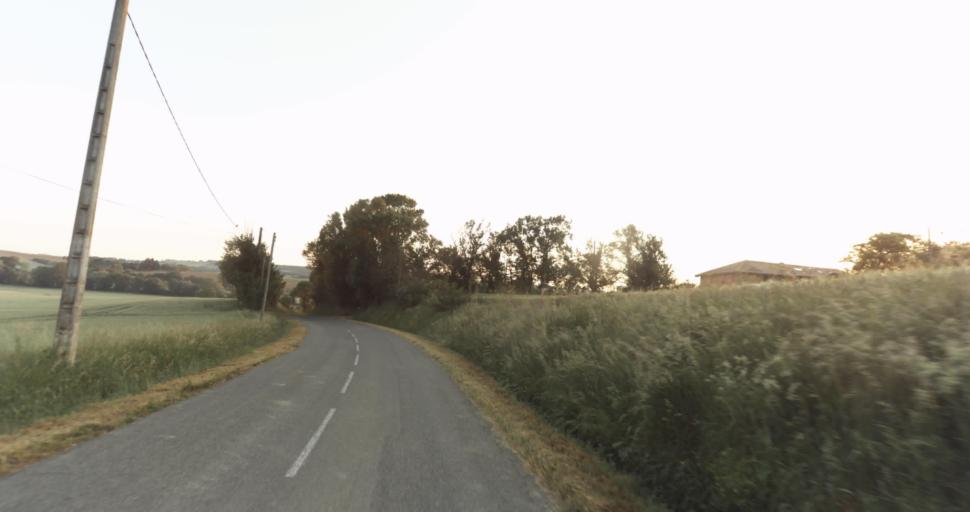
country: FR
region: Midi-Pyrenees
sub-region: Departement du Gers
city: Pujaudran
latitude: 43.6544
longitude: 1.1088
